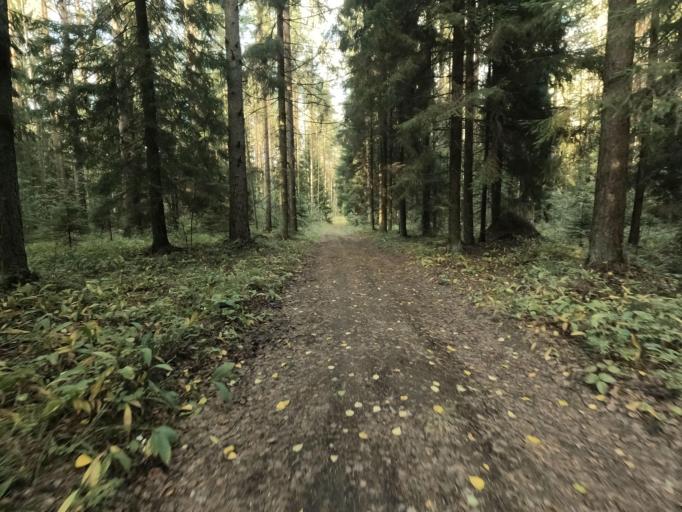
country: RU
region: Leningrad
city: Imeni Sverdlova
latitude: 59.8447
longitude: 30.7299
